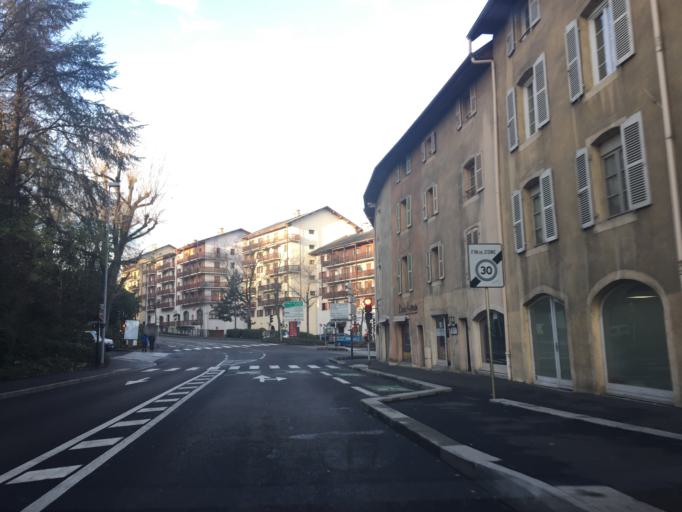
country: FR
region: Rhone-Alpes
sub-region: Departement de la Savoie
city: Jacob-Bellecombette
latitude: 45.5654
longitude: 5.9166
